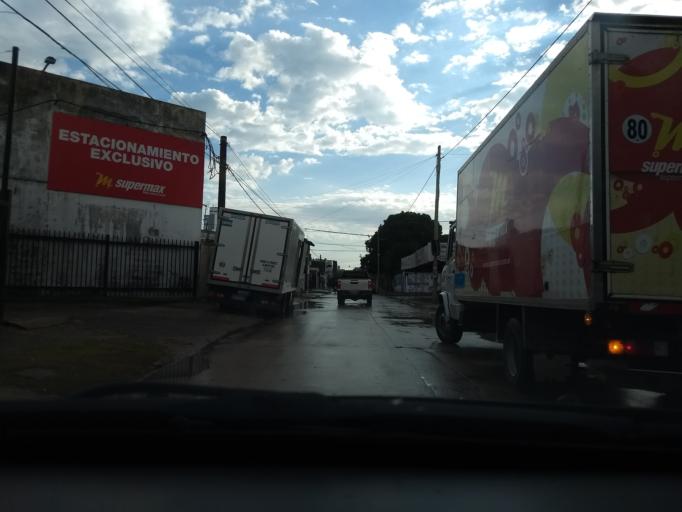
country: AR
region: Corrientes
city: Corrientes
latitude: -27.4781
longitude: -58.8290
